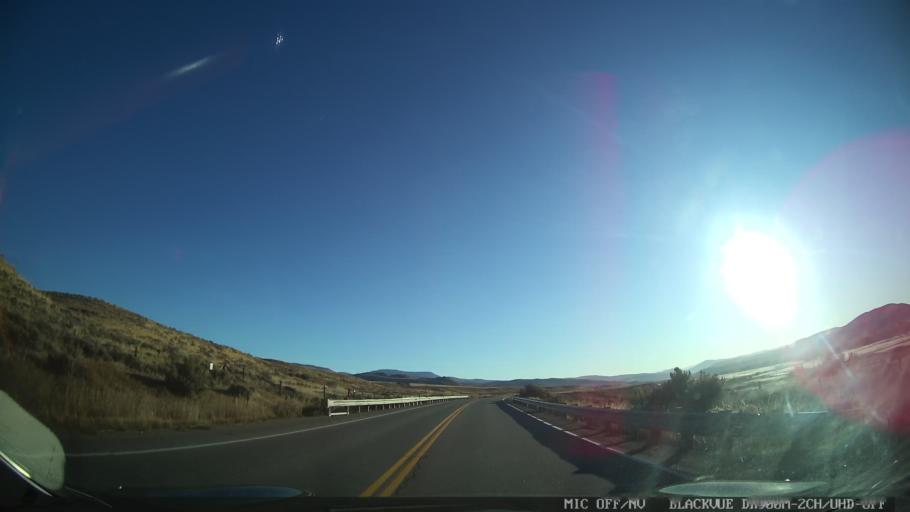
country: US
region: Colorado
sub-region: Grand County
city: Kremmling
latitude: 40.0629
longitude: -106.2970
